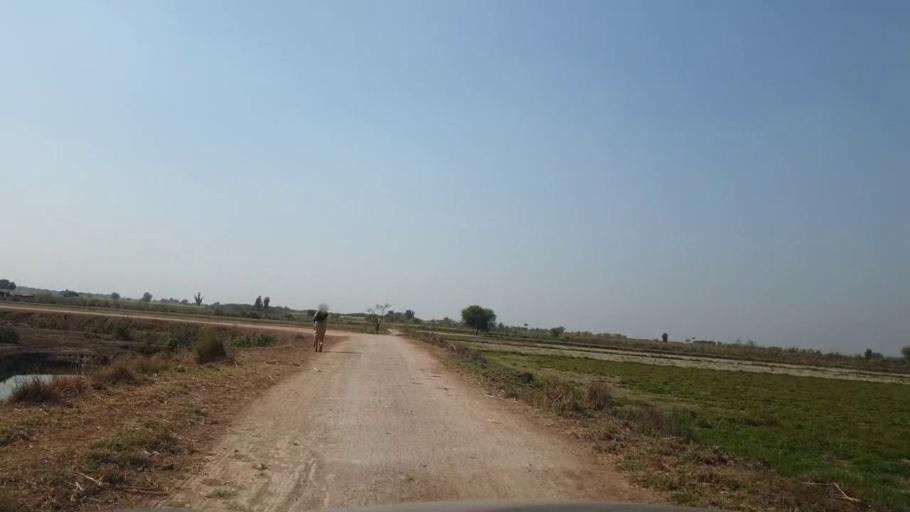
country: PK
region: Sindh
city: Tando Allahyar
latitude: 25.5529
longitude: 68.6989
